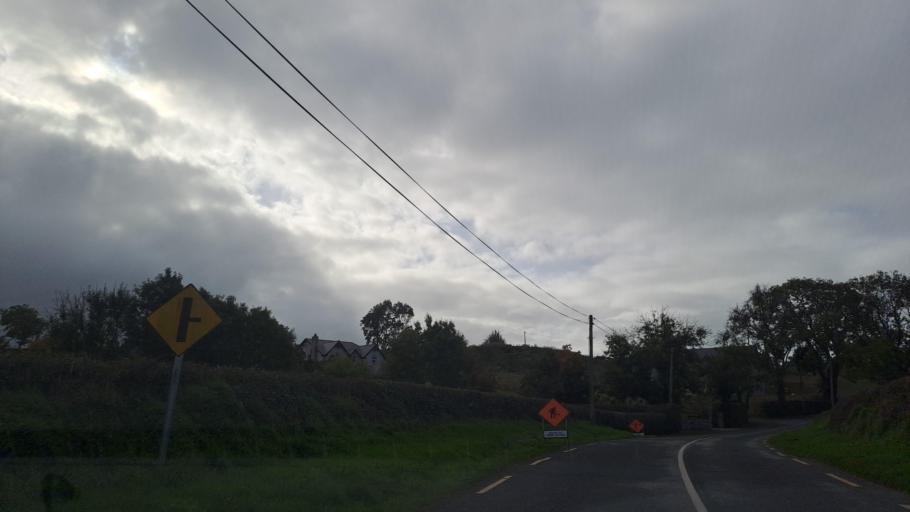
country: IE
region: Ulster
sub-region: County Monaghan
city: Carrickmacross
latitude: 54.0082
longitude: -6.7240
